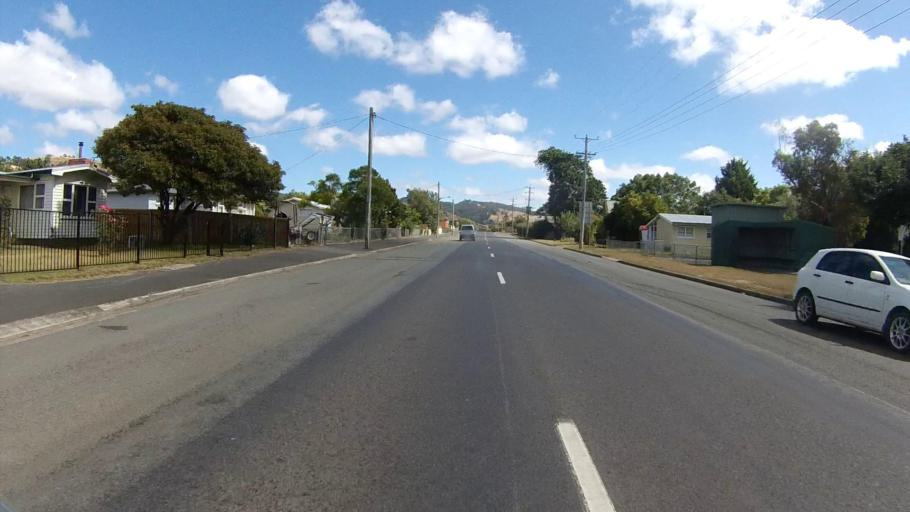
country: AU
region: Tasmania
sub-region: Brighton
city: Bridgewater
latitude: -42.5356
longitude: 147.3652
